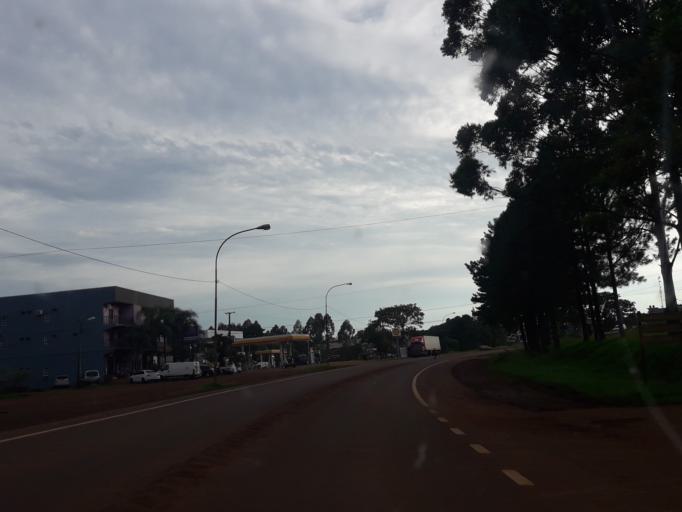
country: AR
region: Misiones
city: Dos de Mayo
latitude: -26.9922
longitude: -54.4896
